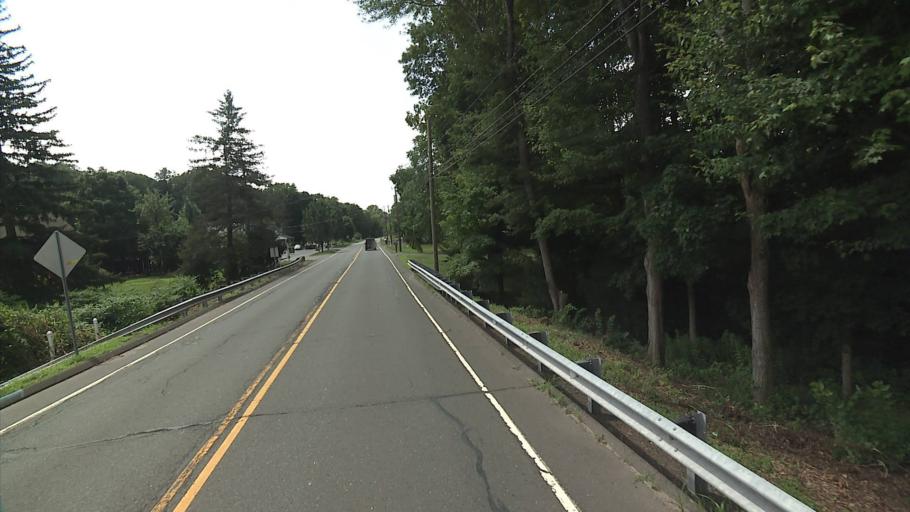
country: US
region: Connecticut
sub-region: Middlesex County
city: Cromwell
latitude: 41.6392
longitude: -72.6057
